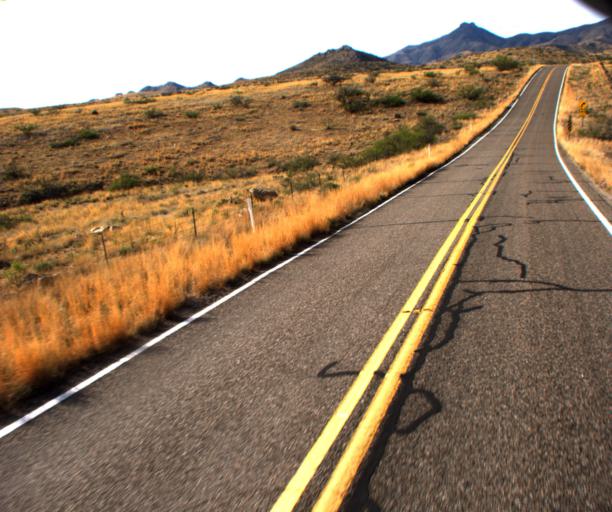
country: US
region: Arizona
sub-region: Cochise County
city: Willcox
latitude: 32.1408
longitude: -109.5647
